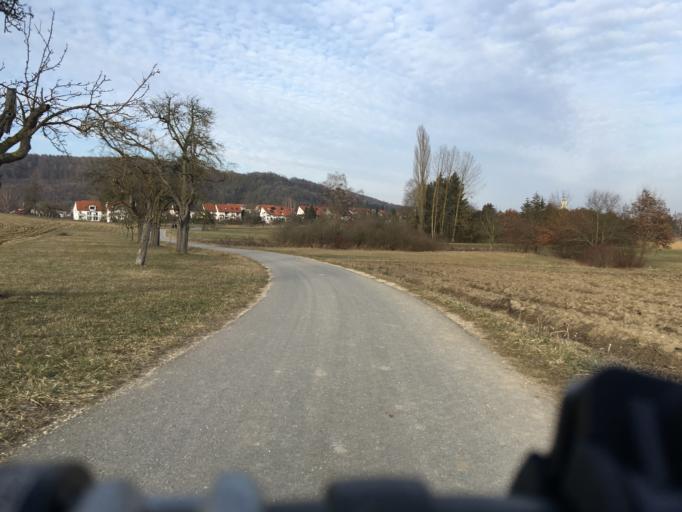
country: DE
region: Baden-Wuerttemberg
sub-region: Freiburg Region
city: Gottmadingen
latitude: 47.7302
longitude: 8.7655
